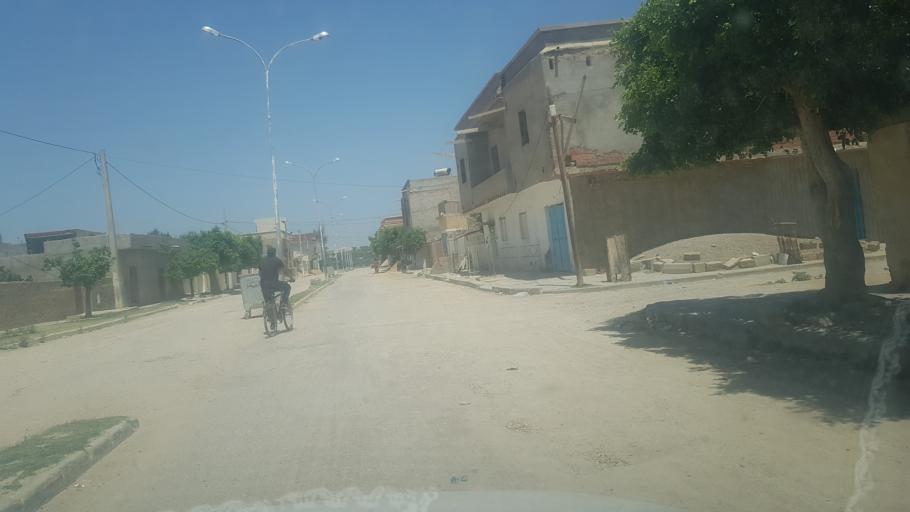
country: TN
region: Al Qayrawan
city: Kairouan
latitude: 35.6214
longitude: 9.9257
